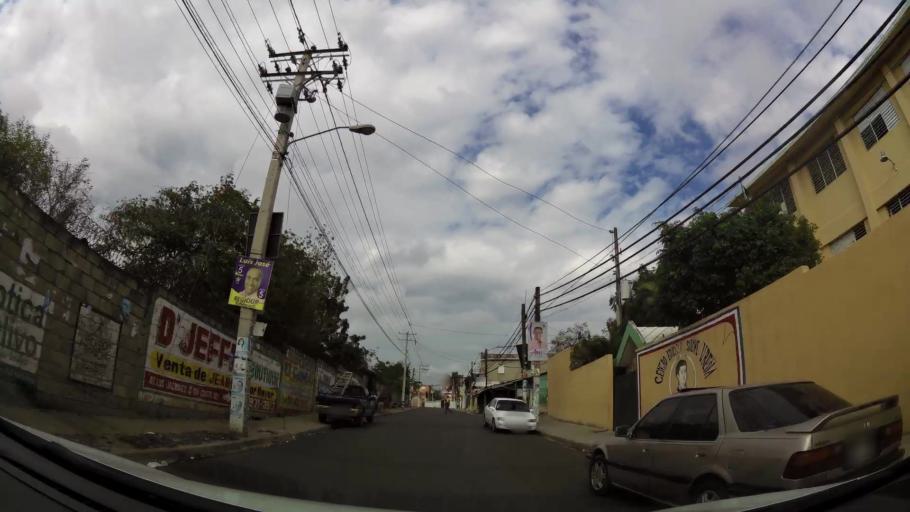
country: DO
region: Santiago
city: Santiago de los Caballeros
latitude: 19.4283
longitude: -70.6801
